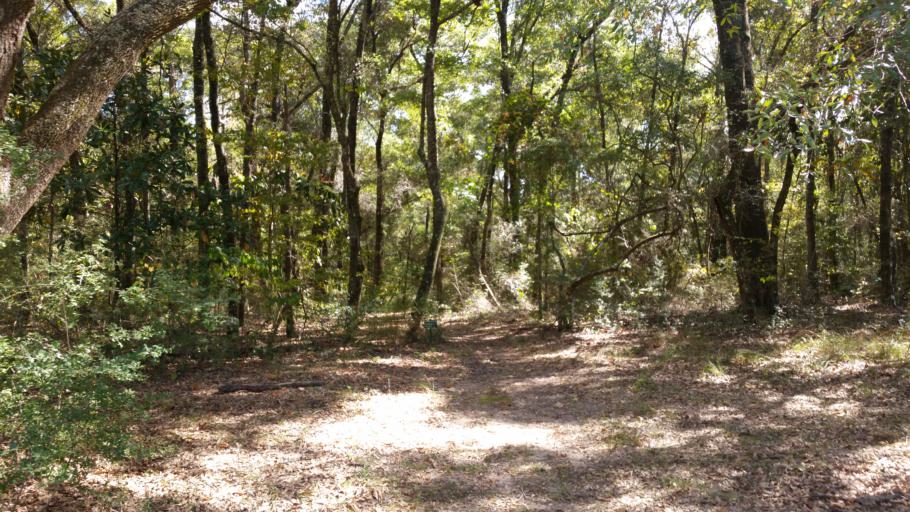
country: US
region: Alabama
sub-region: Baldwin County
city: Spanish Fort
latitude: 30.7417
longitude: -87.9245
